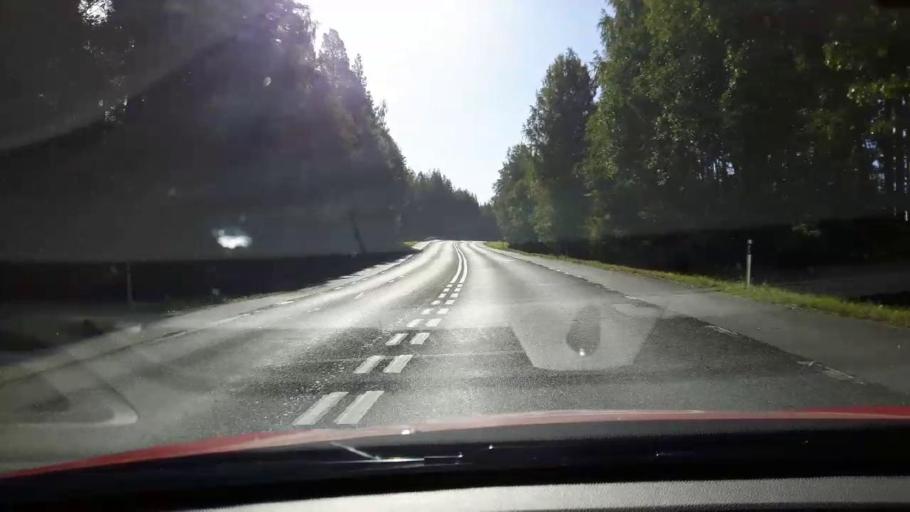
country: SE
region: Jaemtland
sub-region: Braecke Kommun
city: Braecke
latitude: 62.7389
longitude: 15.4291
